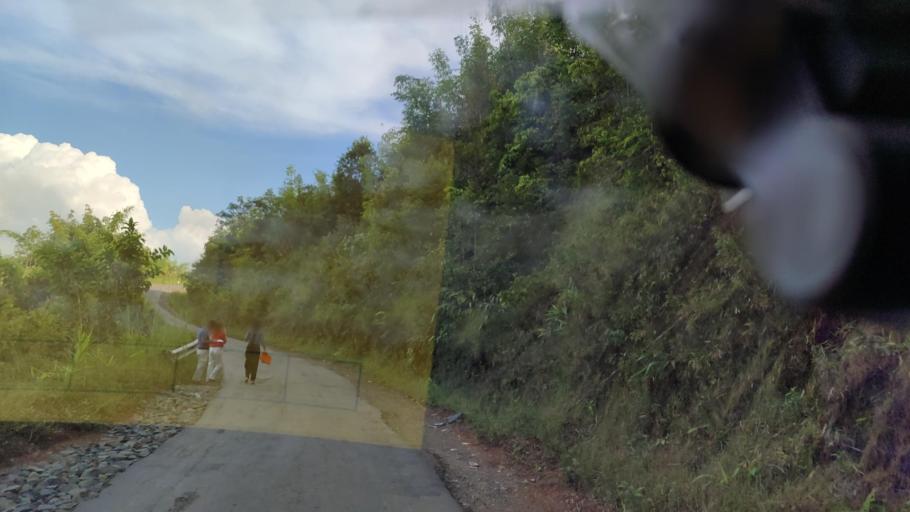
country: MM
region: Magway
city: Minbu
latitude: 19.8692
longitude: 94.1753
